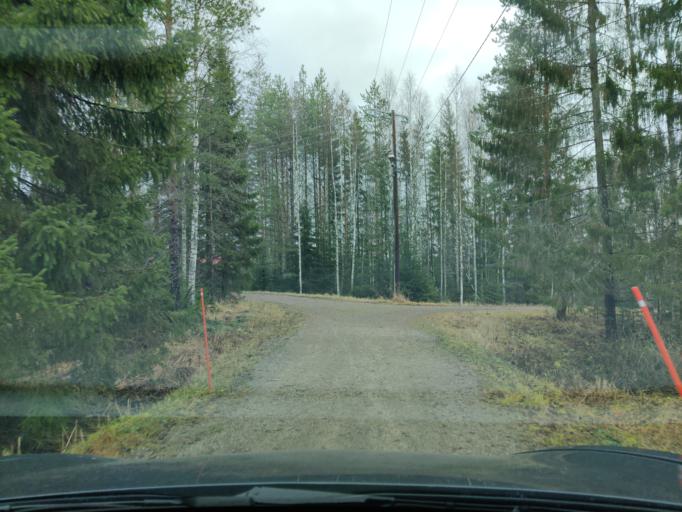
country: FI
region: Northern Savo
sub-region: Ylae-Savo
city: Kiuruvesi
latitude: 63.6413
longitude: 26.6412
